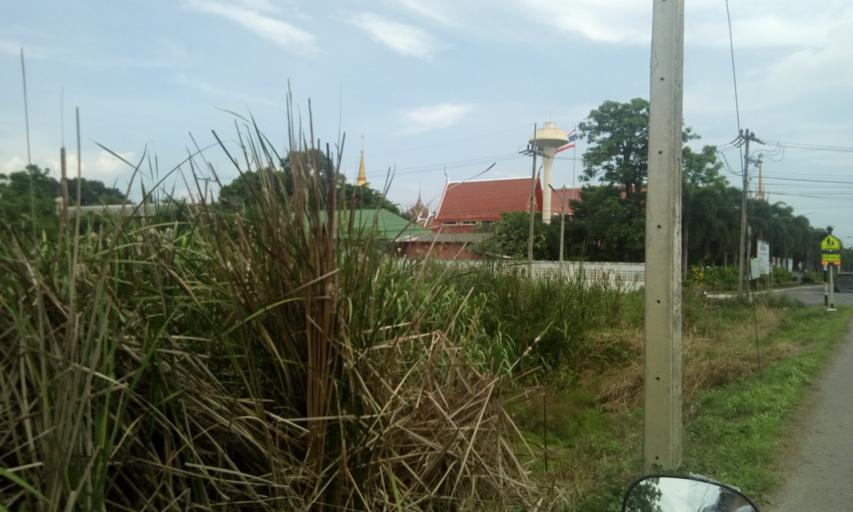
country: TH
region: Pathum Thani
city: Ban Lam Luk Ka
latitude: 14.0204
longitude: 100.8435
